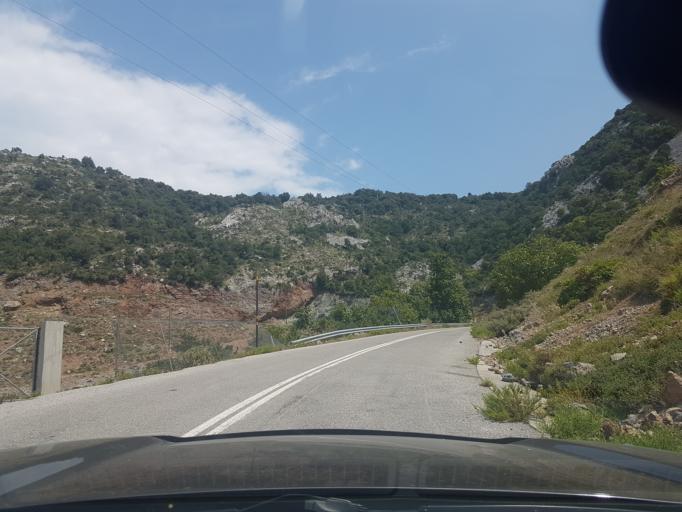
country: GR
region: Central Greece
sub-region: Nomos Evvoias
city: Kymi
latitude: 38.6519
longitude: 23.9670
